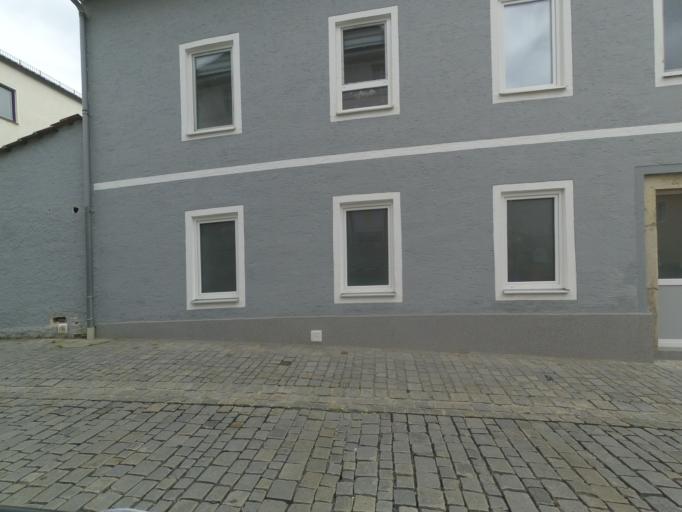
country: DE
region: Bavaria
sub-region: Lower Bavaria
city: Regen
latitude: 48.9703
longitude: 13.1255
